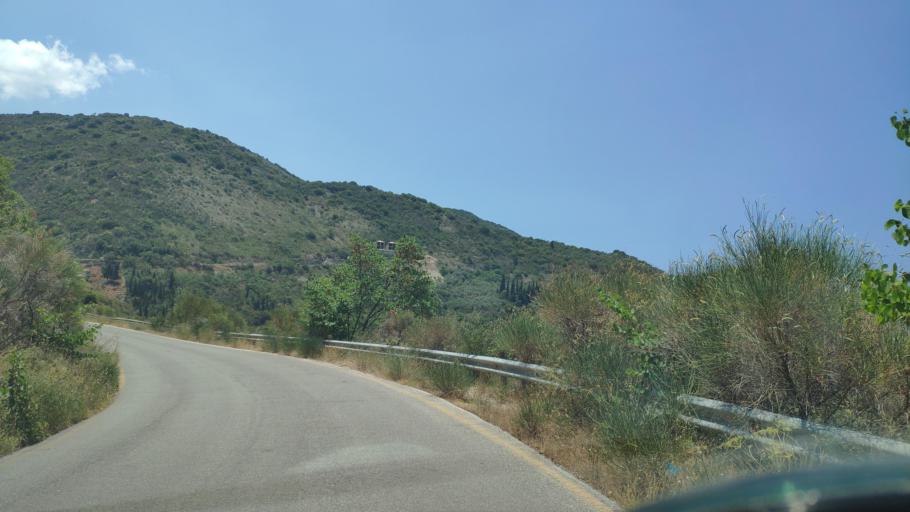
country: GR
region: Ionian Islands
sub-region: Lefkada
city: Nidri
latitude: 38.7488
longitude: 20.6204
